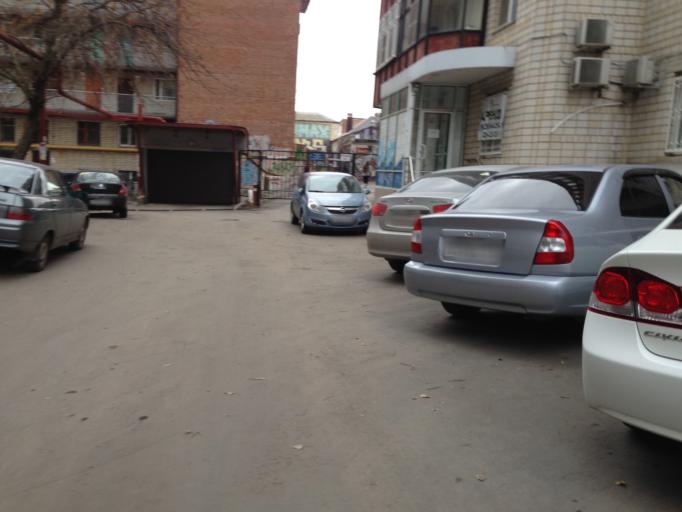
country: RU
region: Rostov
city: Rostov-na-Donu
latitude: 47.2230
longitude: 39.7280
